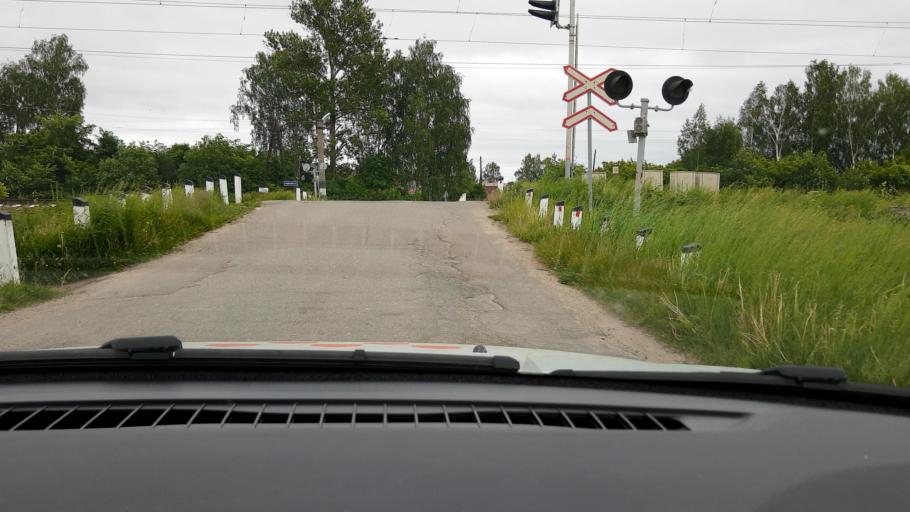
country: RU
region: Nizjnij Novgorod
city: Sitniki
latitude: 56.5200
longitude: 44.0490
